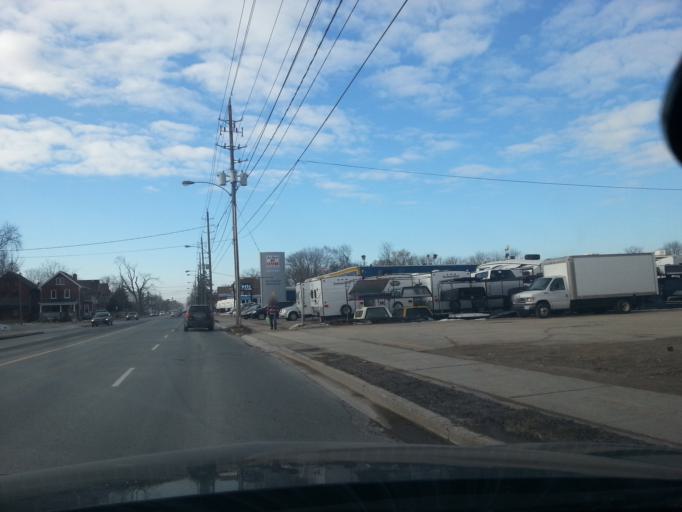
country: CA
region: Ontario
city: Peterborough
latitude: 44.2906
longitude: -78.3105
